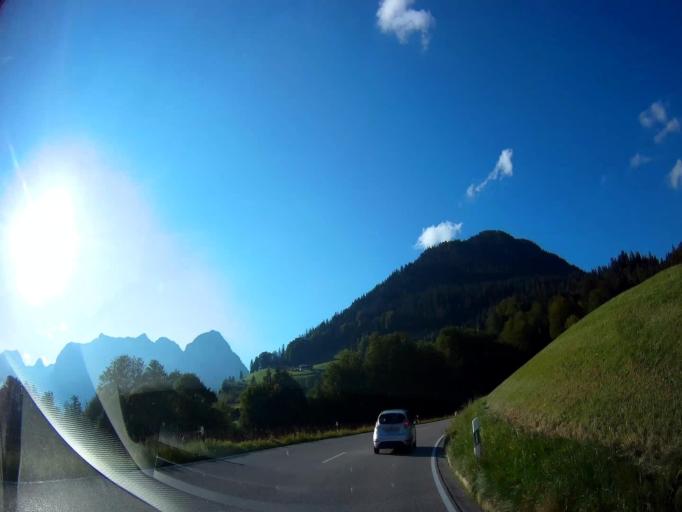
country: DE
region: Bavaria
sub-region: Upper Bavaria
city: Ramsau
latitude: 47.6136
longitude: 12.8997
